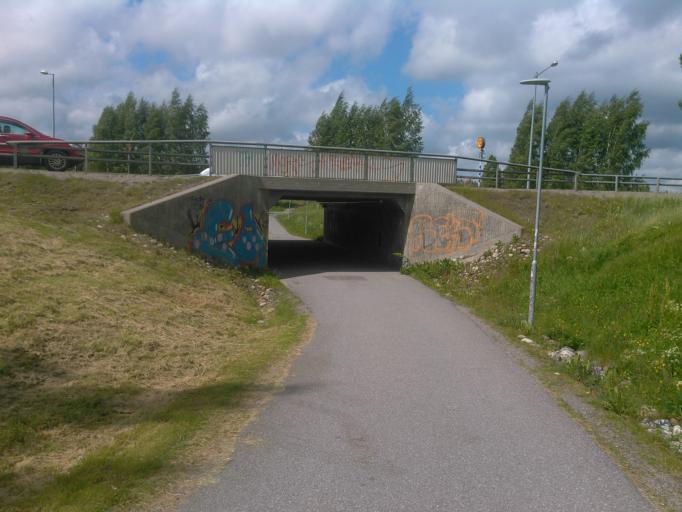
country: SE
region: Vaesterbotten
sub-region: Umea Kommun
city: Umea
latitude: 63.8370
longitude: 20.2719
